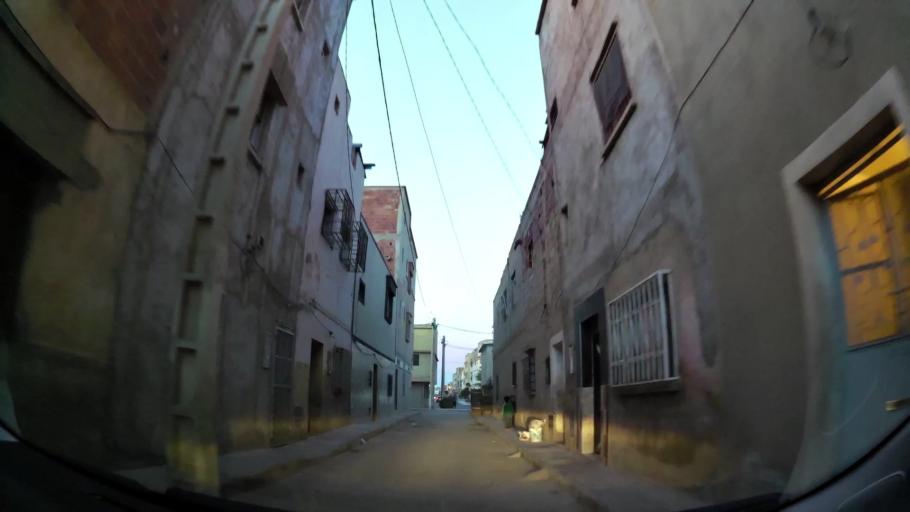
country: MA
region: Oriental
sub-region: Oujda-Angad
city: Oujda
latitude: 34.6829
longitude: -1.8758
